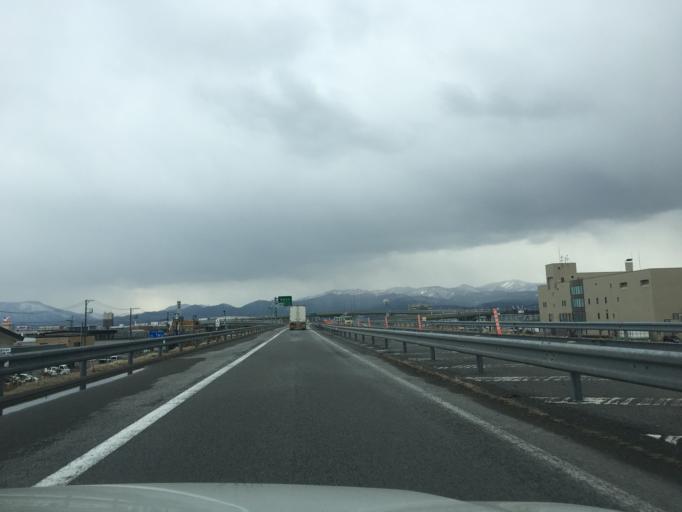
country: JP
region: Aomori
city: Aomori Shi
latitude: 40.7969
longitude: 140.7367
